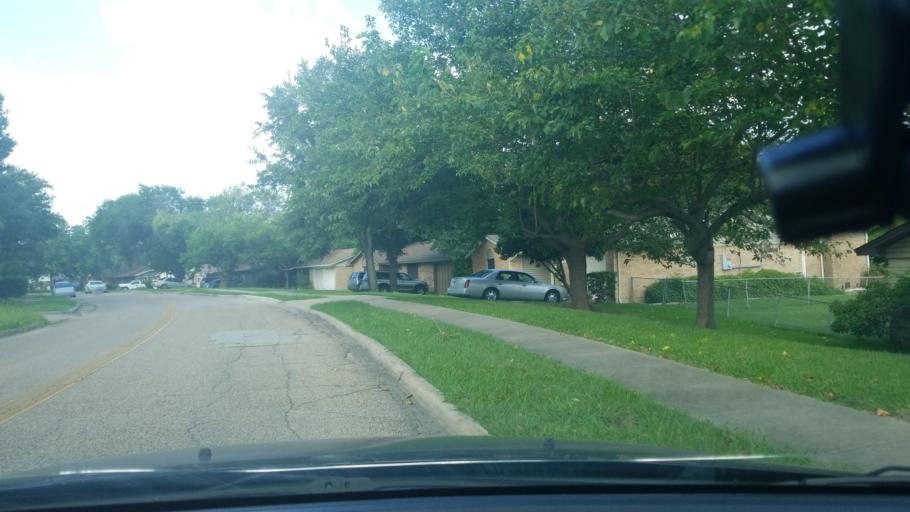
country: US
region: Texas
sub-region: Dallas County
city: Mesquite
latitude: 32.7734
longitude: -96.6354
